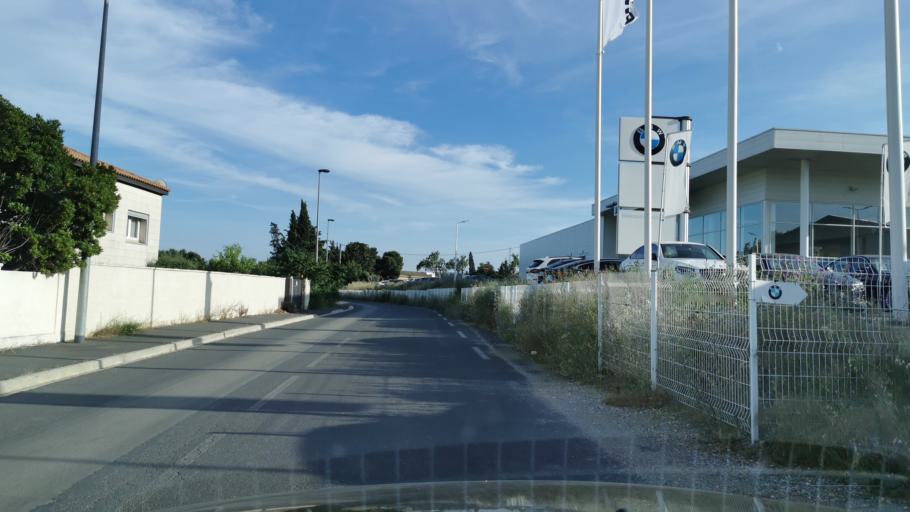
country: FR
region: Languedoc-Roussillon
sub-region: Departement de l'Aude
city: Narbonne
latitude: 43.1724
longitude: 2.9924
